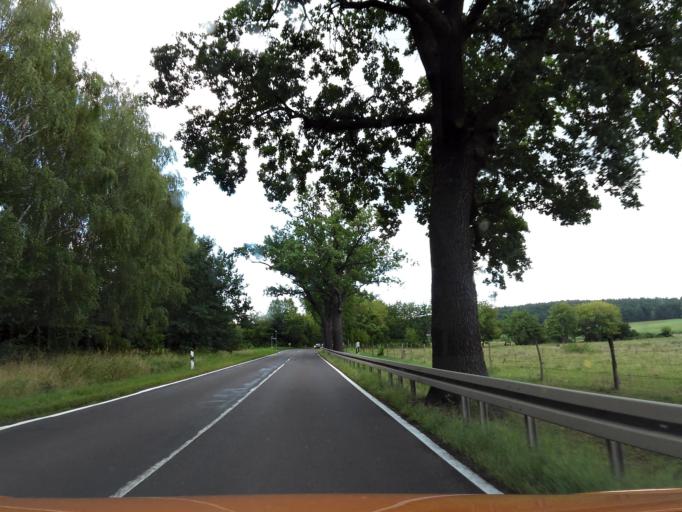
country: DE
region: Brandenburg
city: Potsdam
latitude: 52.4594
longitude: 13.0362
